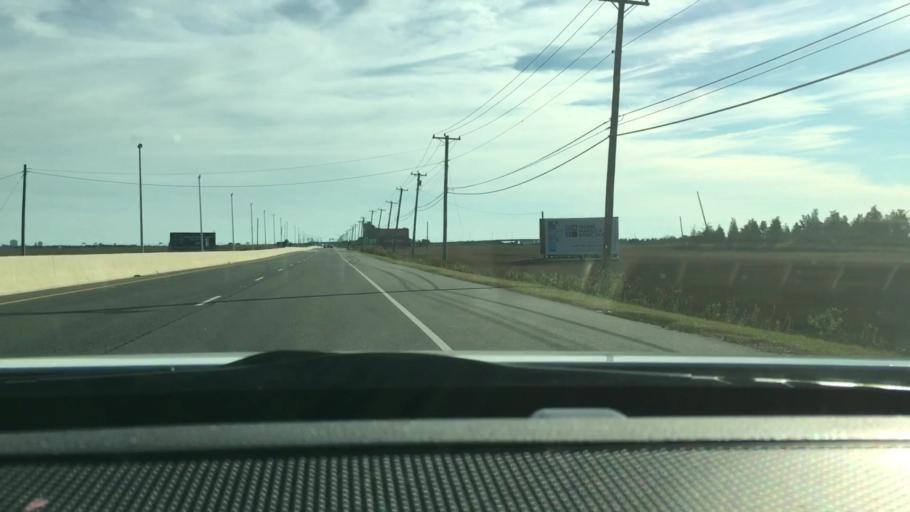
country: US
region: New Jersey
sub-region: Atlantic County
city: Absecon
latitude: 39.4131
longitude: -74.4916
